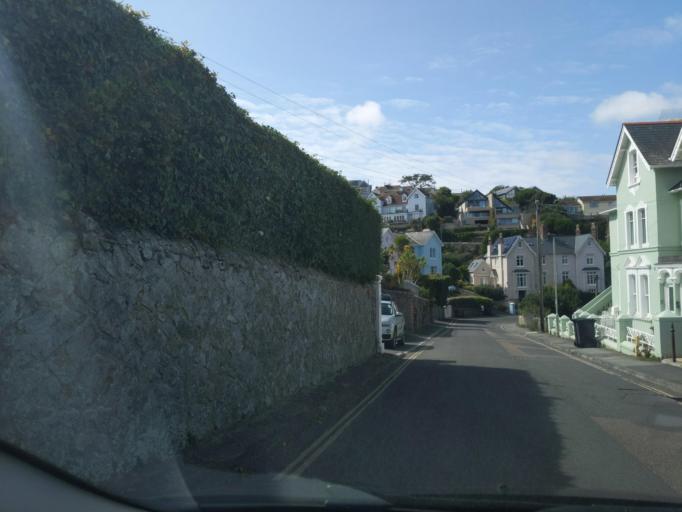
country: GB
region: England
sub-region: Devon
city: Salcombe
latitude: 50.2370
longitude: -3.7685
